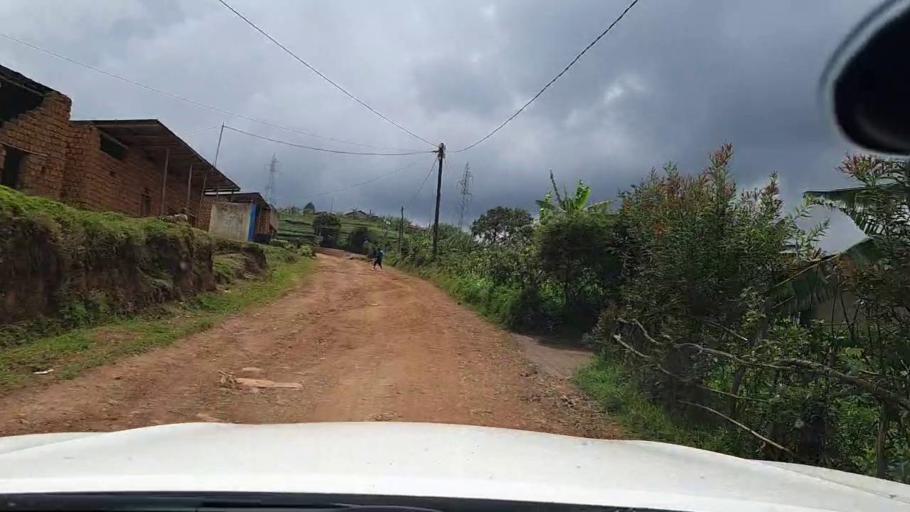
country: RW
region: Western Province
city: Kibuye
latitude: -2.1702
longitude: 29.4320
